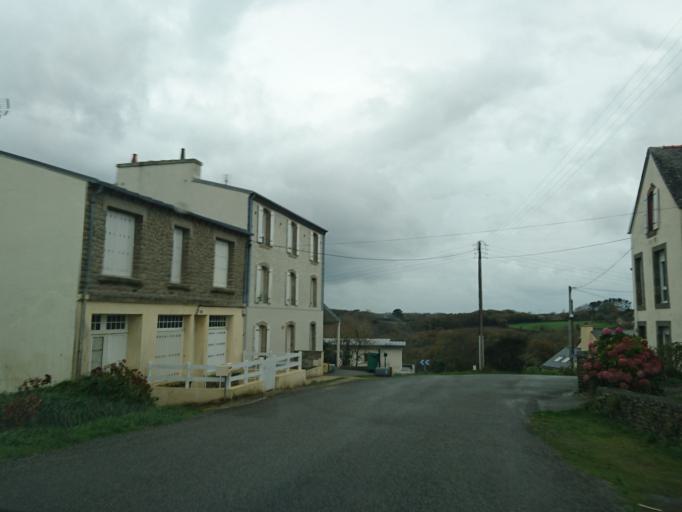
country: FR
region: Brittany
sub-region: Departement du Finistere
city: Plougonvelin
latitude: 48.3605
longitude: -4.6756
